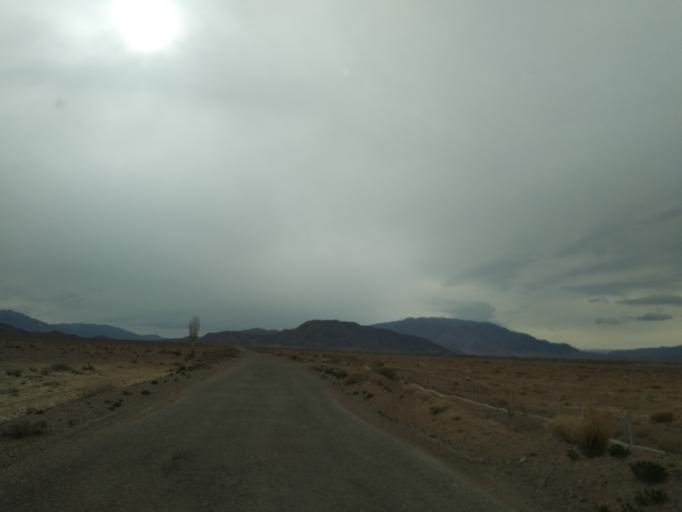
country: KG
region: Ysyk-Koel
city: Balykchy
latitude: 42.3208
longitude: 76.2190
